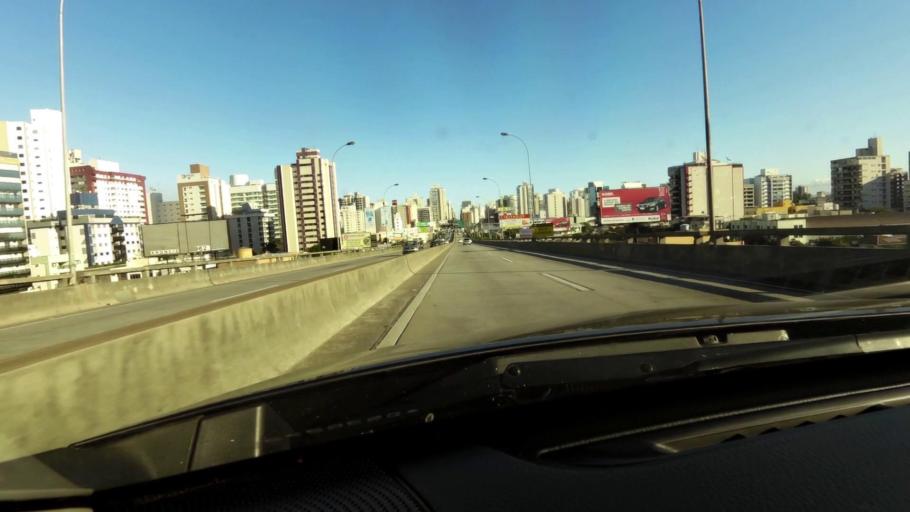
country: BR
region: Espirito Santo
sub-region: Vila Velha
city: Vila Velha
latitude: -20.3328
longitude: -40.2840
